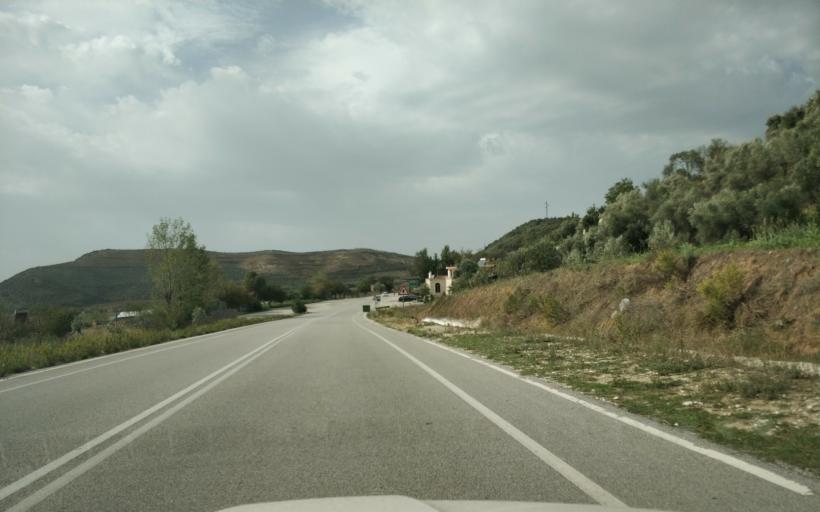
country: AL
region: Gjirokaster
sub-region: Rrethi i Tepelenes
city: Krahes
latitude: 40.3874
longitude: 19.8829
